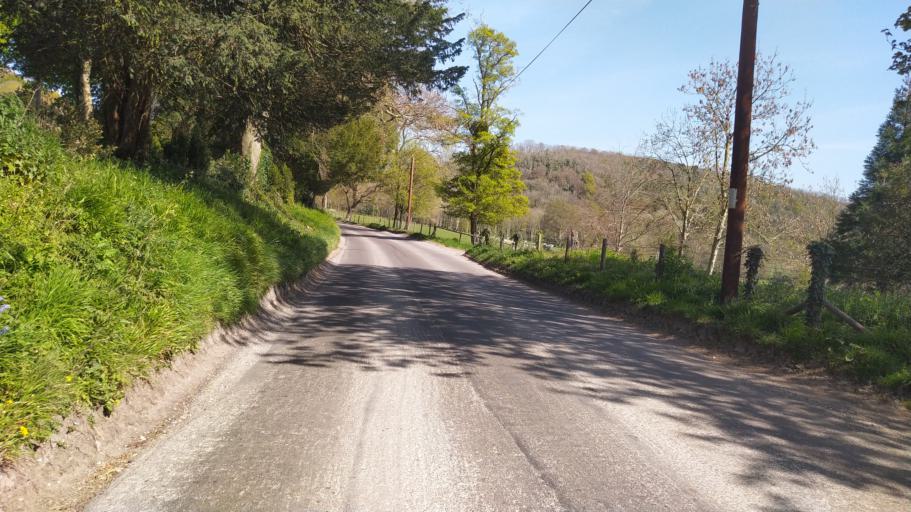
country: GB
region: England
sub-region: Dorset
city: Manston
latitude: 50.9008
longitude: -2.2181
